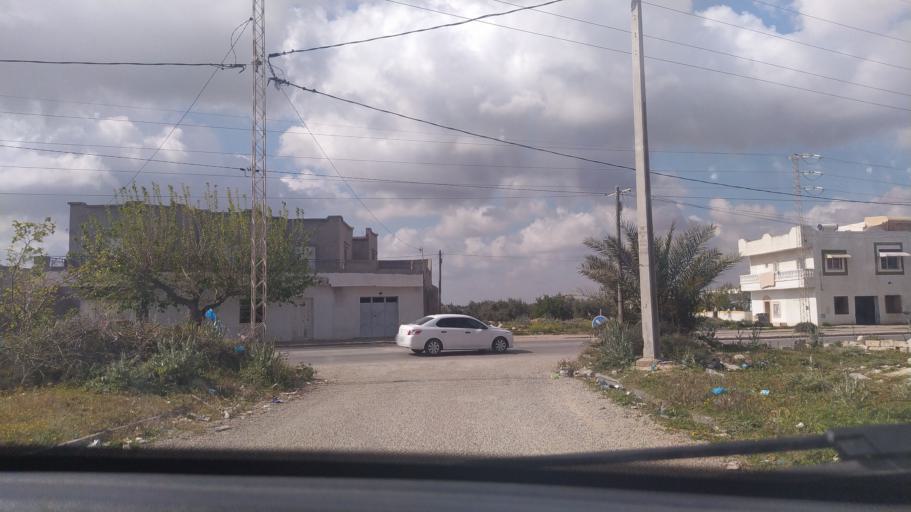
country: TN
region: Al Munastir
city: Sidi Bin Nur
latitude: 35.5237
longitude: 10.9390
